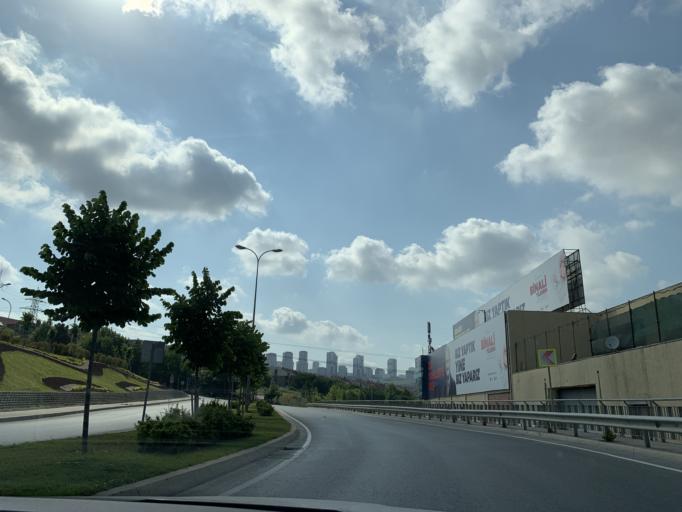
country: TR
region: Istanbul
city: Esenyurt
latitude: 41.0813
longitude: 28.6793
